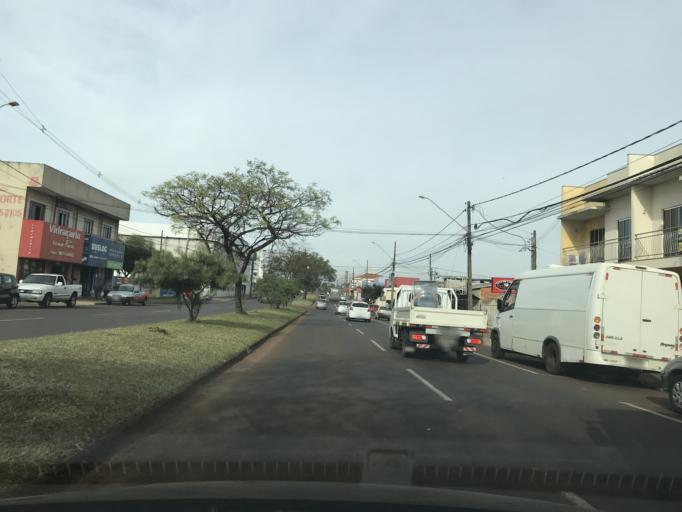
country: BR
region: Parana
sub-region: Cascavel
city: Cascavel
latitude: -24.9655
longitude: -53.4833
